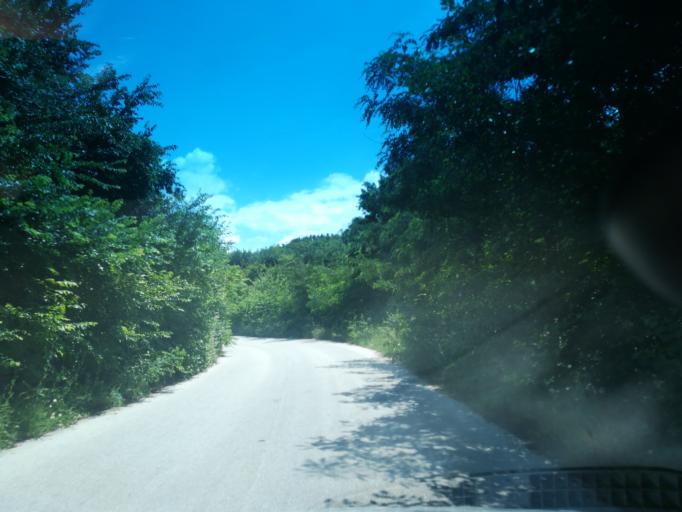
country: BG
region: Khaskovo
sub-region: Obshtina Mineralni Bani
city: Mineralni Bani
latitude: 41.9818
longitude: 25.2453
